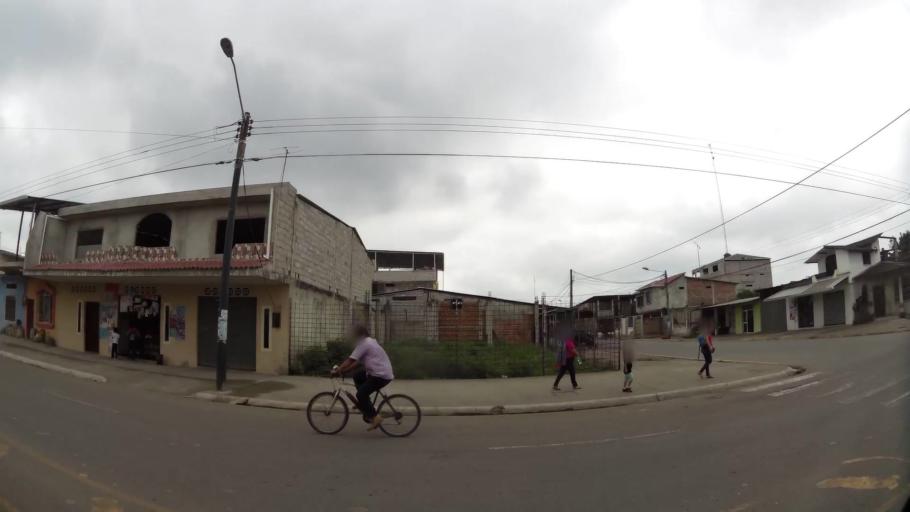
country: EC
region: El Oro
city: Pasaje
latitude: -3.2412
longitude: -79.8329
